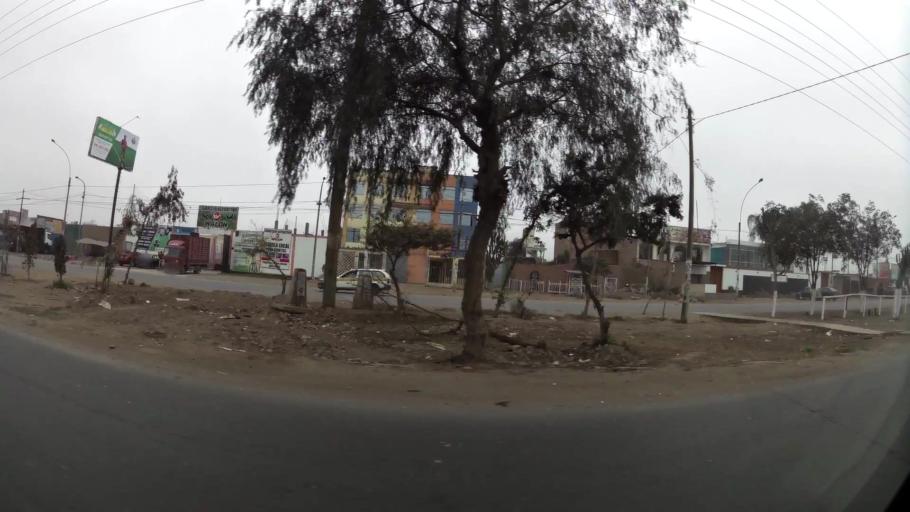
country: PE
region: Lima
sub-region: Lima
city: Urb. Santo Domingo
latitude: -11.9189
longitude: -77.0607
